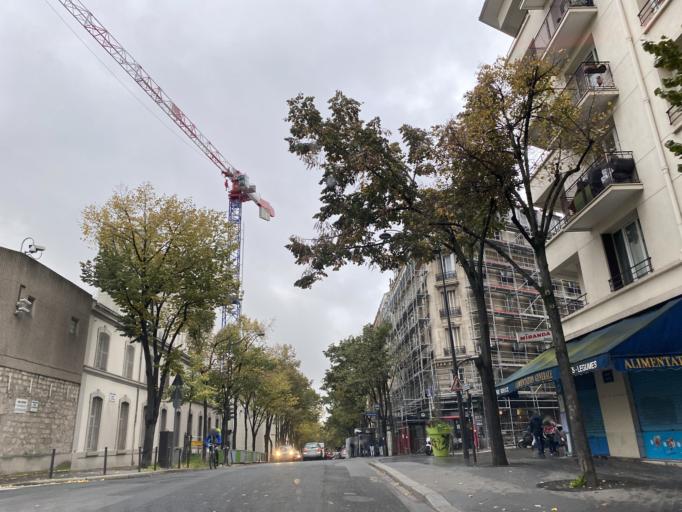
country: FR
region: Ile-de-France
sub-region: Departement de Seine-Saint-Denis
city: Le Pre-Saint-Gervais
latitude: 48.8752
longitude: 2.4057
